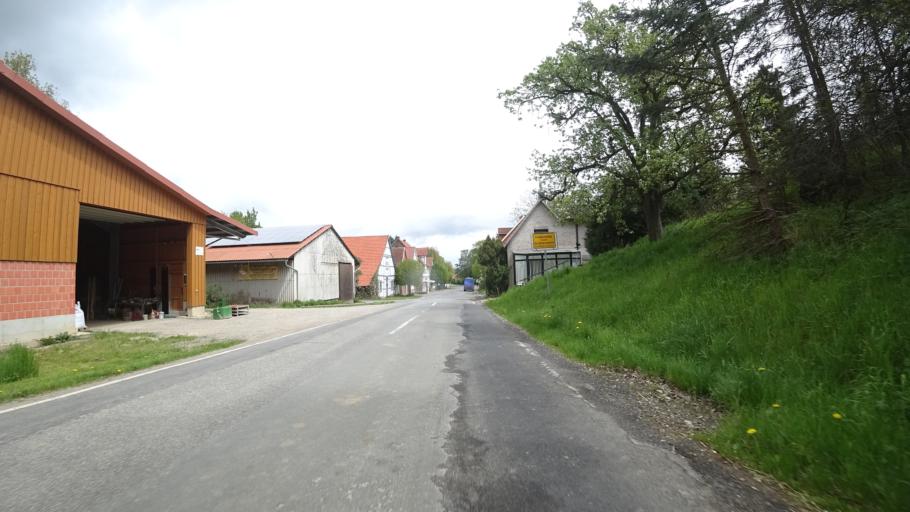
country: DE
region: Hesse
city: Grebenstein
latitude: 51.4436
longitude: 9.3639
